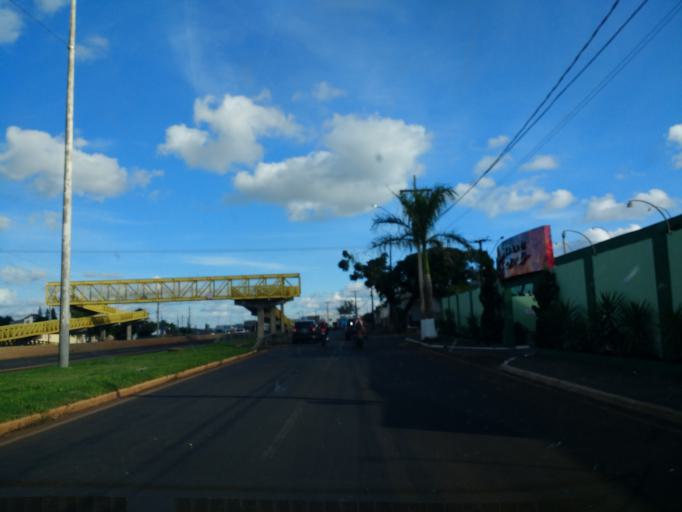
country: BR
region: Parana
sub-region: Cambe
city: Cambe
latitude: -23.2891
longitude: -51.2353
